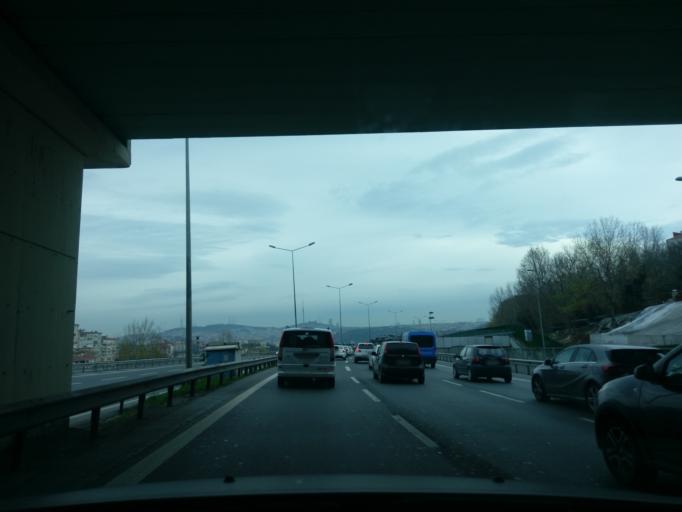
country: TR
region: Istanbul
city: Sisli
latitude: 41.0654
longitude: 29.0142
